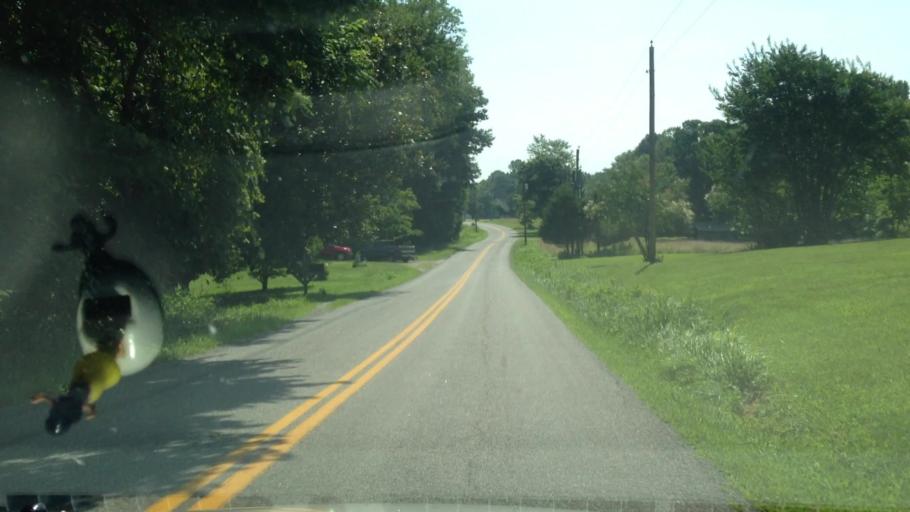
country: US
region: Virginia
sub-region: Patrick County
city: Stuart
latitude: 36.5789
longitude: -80.2645
